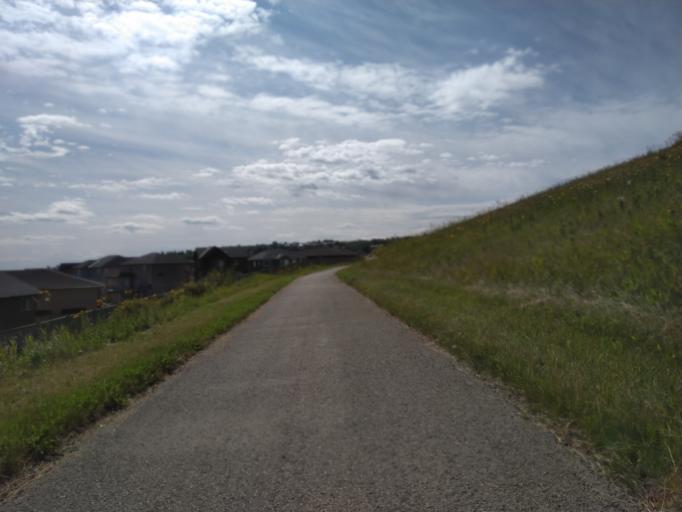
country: CA
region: Alberta
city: Calgary
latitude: 51.1559
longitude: -114.1533
